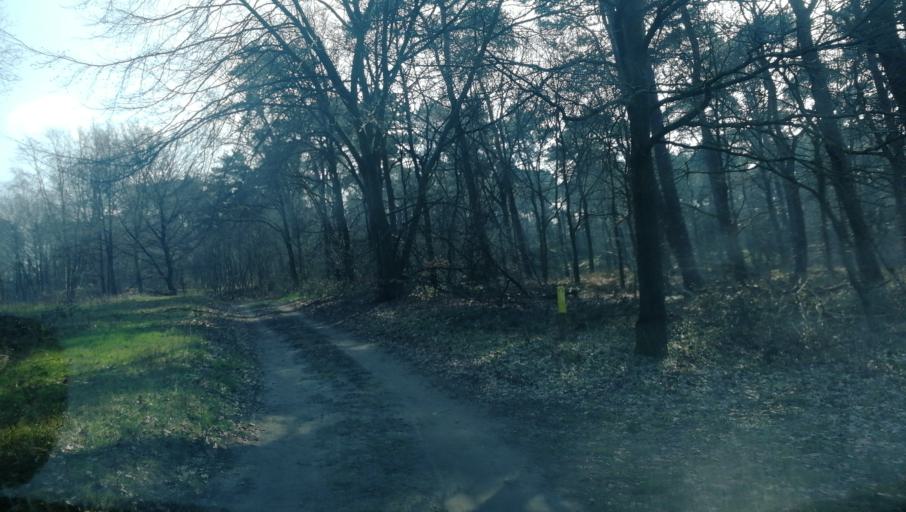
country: NL
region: Limburg
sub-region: Gemeente Venlo
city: Venlo
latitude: 51.3973
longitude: 6.1836
